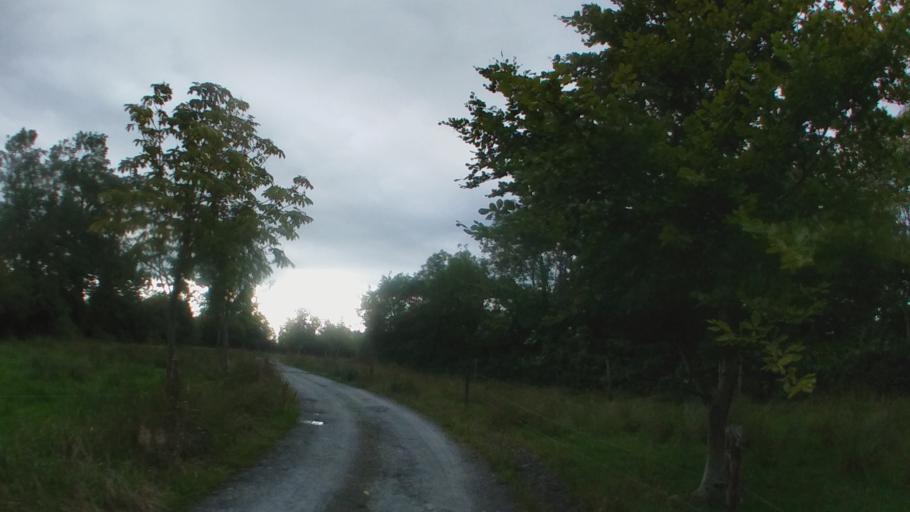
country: IE
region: Leinster
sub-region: Kilkenny
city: Kilkenny
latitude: 52.6776
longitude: -7.2214
